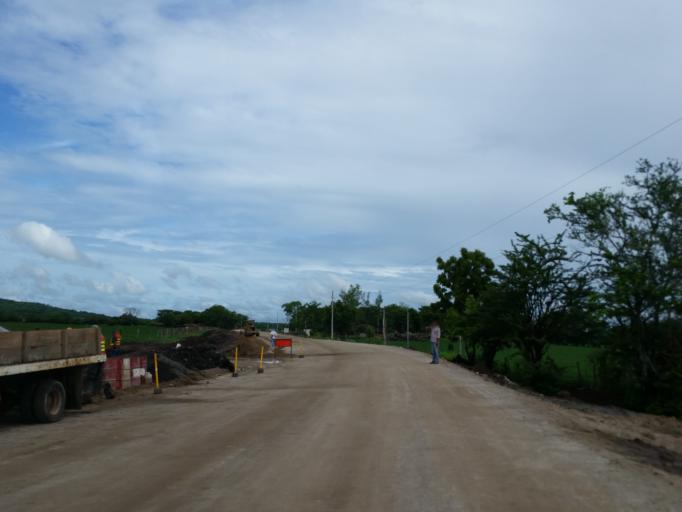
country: NI
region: Leon
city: Larreynaga
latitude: 12.5455
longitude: -86.6165
